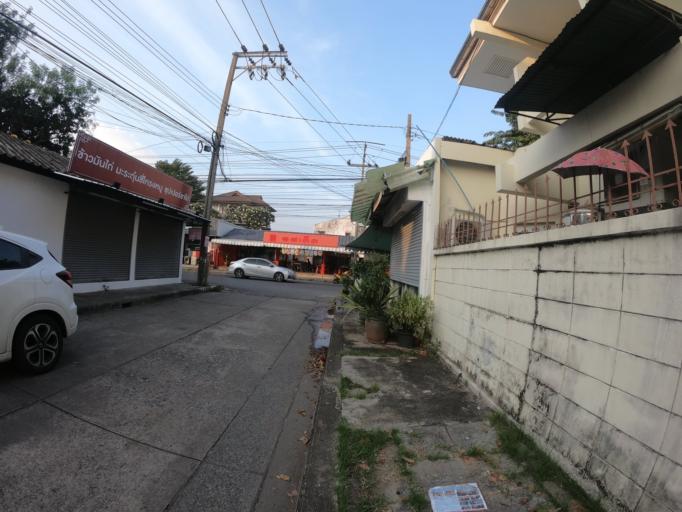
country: TH
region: Bangkok
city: Lat Phrao
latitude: 13.8311
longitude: 100.6062
